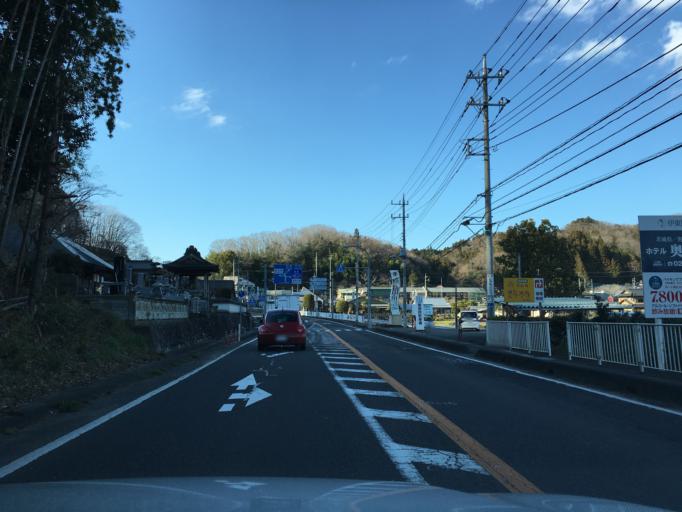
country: JP
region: Ibaraki
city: Daigo
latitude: 36.7565
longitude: 140.3827
